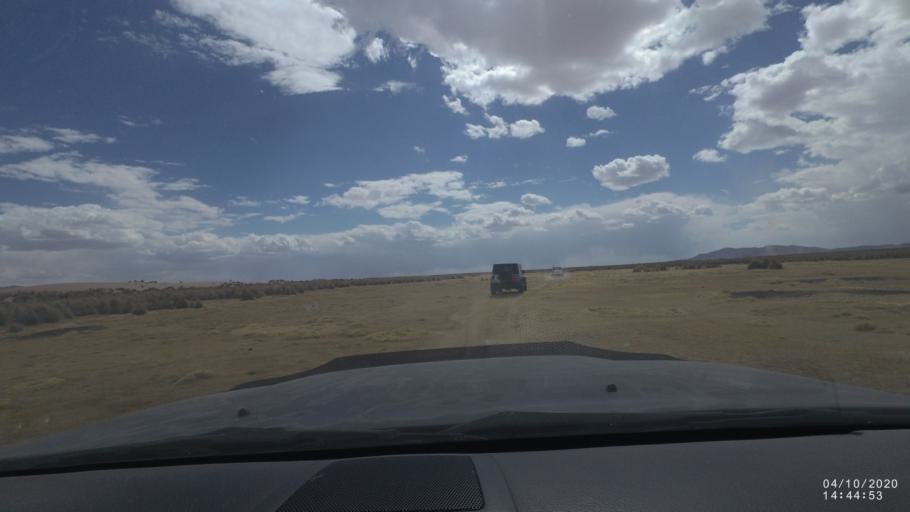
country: BO
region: Oruro
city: Poopo
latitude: -18.6868
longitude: -67.4969
